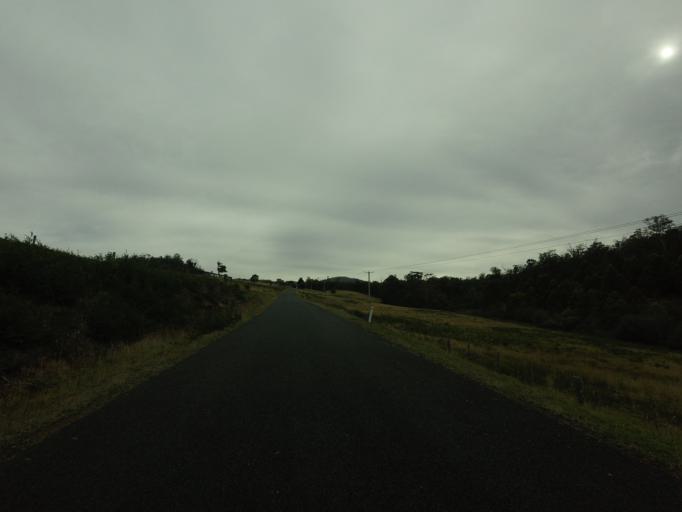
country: AU
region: Tasmania
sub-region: Sorell
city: Sorell
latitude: -42.5476
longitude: 147.5678
